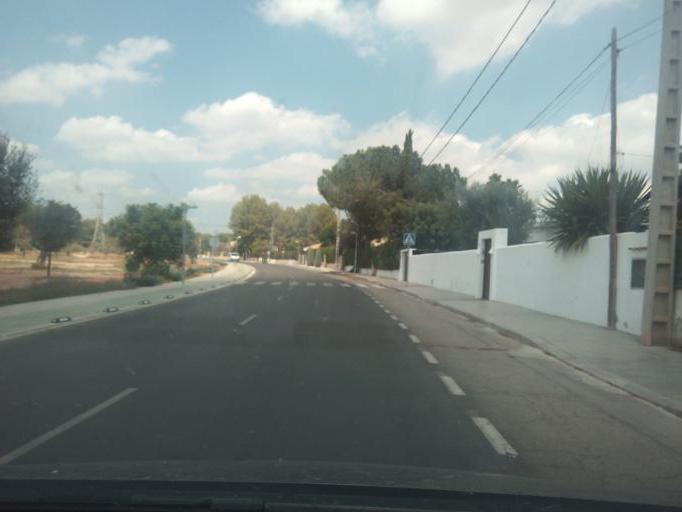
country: ES
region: Valencia
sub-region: Provincia de Valencia
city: L'Eliana
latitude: 39.5374
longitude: -0.4903
